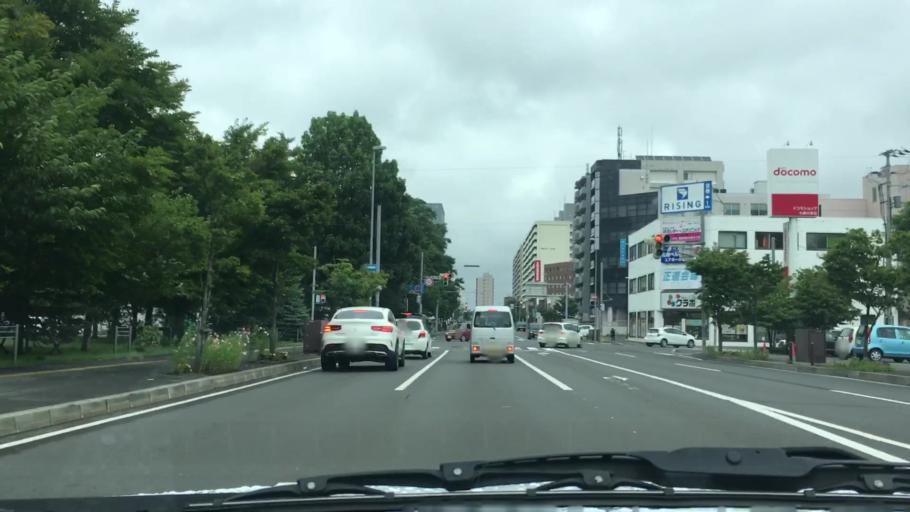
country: JP
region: Hokkaido
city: Sapporo
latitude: 43.0717
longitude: 141.3653
